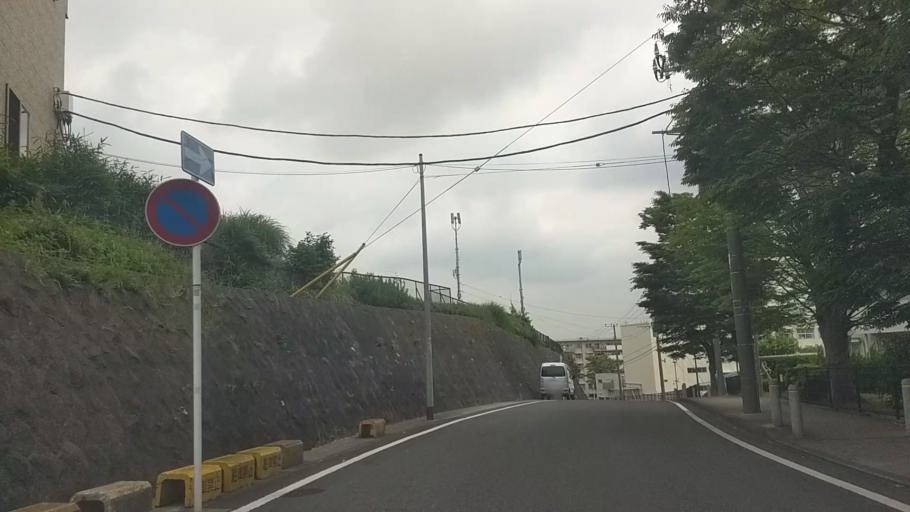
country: JP
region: Kanagawa
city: Kamakura
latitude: 35.3719
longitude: 139.5339
